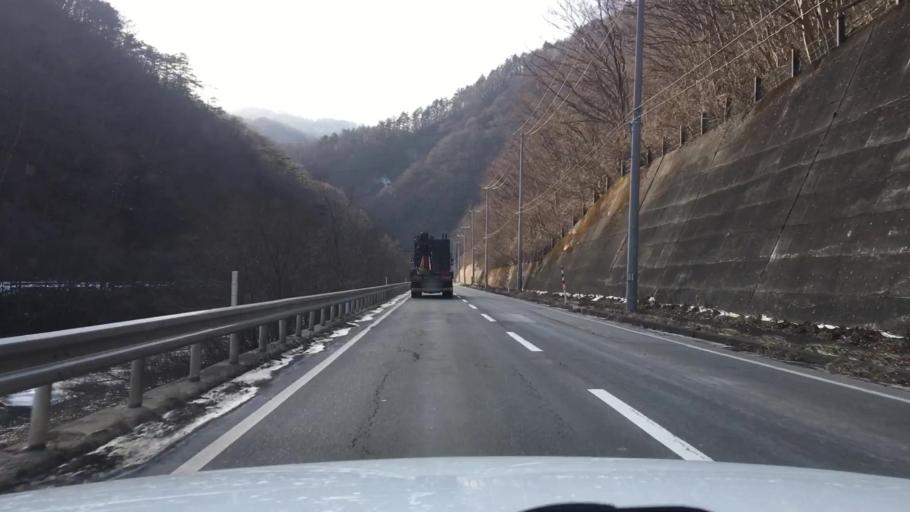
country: JP
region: Iwate
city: Tono
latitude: 39.6490
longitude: 141.5764
